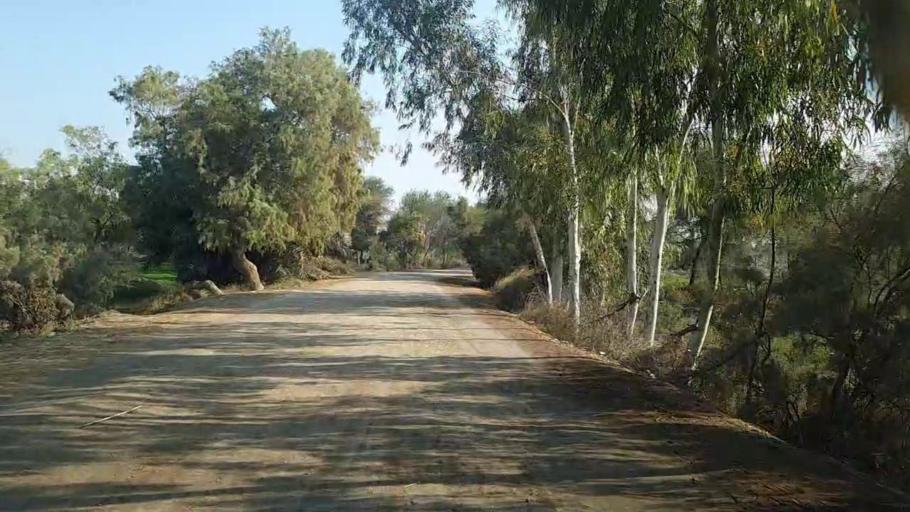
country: PK
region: Sindh
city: Mirpur Mathelo
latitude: 27.8885
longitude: 69.6096
